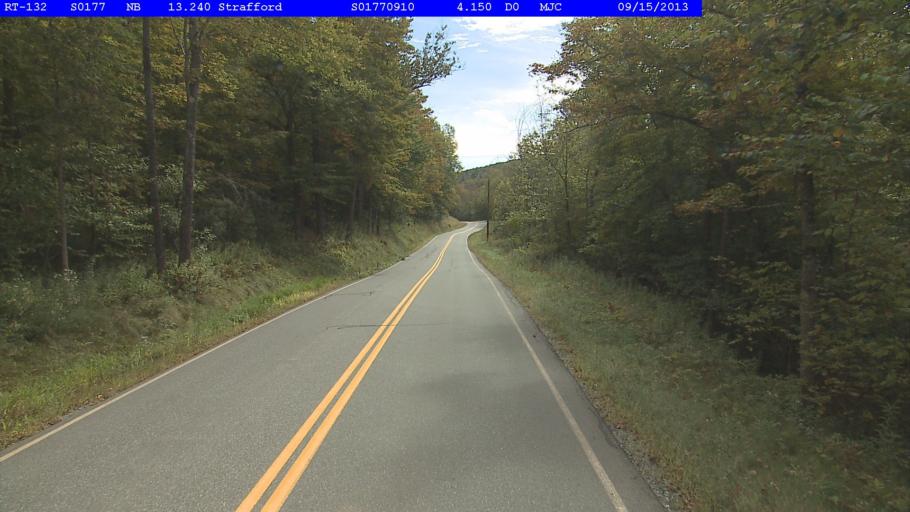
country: US
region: New Hampshire
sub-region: Grafton County
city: Hanover
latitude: 43.8341
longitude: -72.3307
